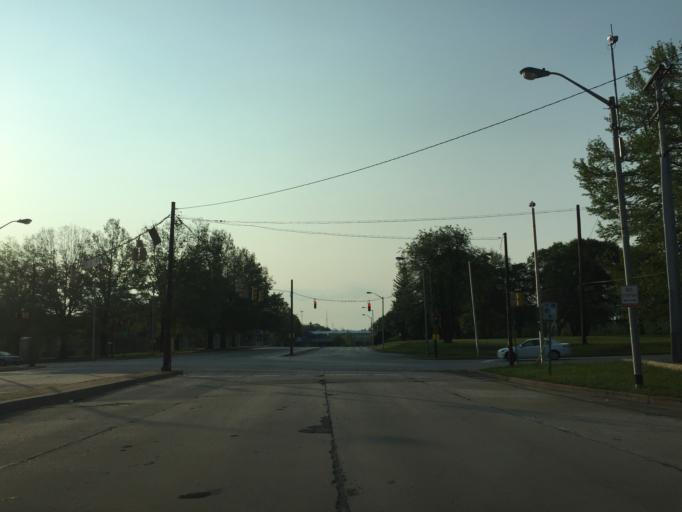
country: US
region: Maryland
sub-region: Baltimore County
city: Lochearn
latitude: 39.3527
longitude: -76.7077
